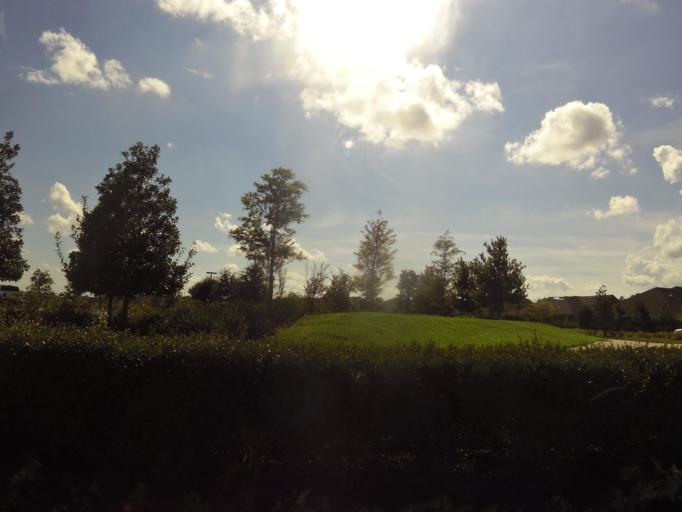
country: US
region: Florida
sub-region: Saint Johns County
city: Palm Valley
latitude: 30.0741
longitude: -81.4703
